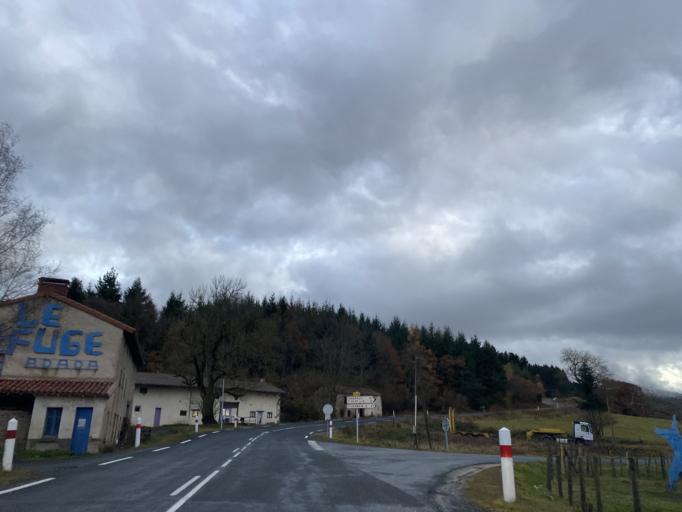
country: FR
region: Auvergne
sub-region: Departement du Puy-de-Dome
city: Cunlhat
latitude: 45.6007
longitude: 3.5599
